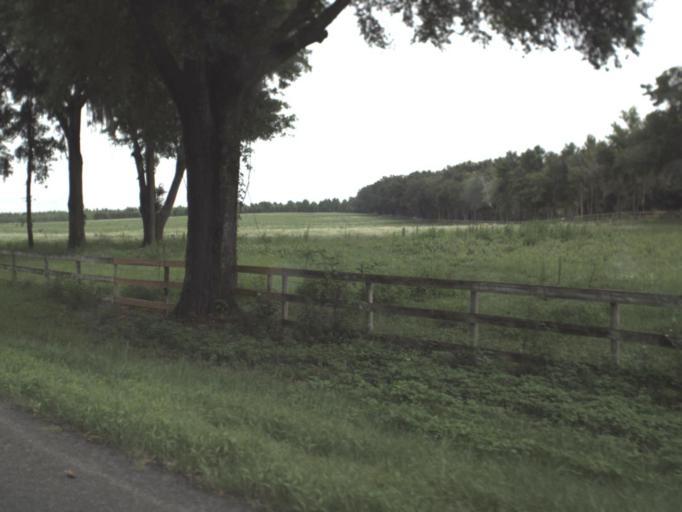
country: US
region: Florida
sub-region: Alachua County
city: Archer
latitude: 29.5772
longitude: -82.5488
